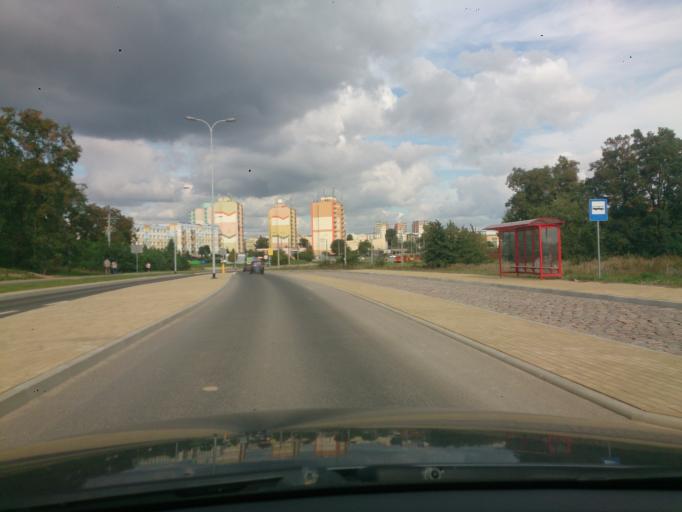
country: PL
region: Kujawsko-Pomorskie
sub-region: Grudziadz
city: Grudziadz
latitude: 53.4481
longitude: 18.7153
